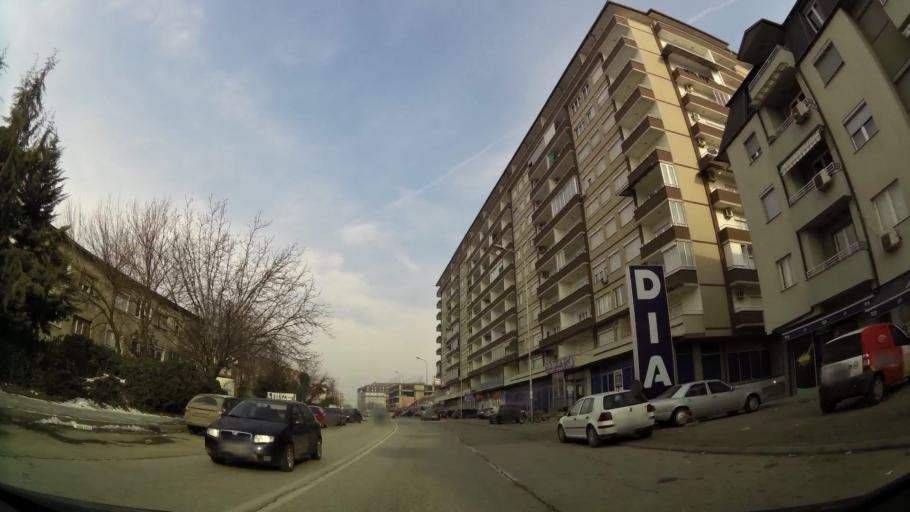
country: MK
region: Cair
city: Cair
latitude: 42.0167
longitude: 21.4362
